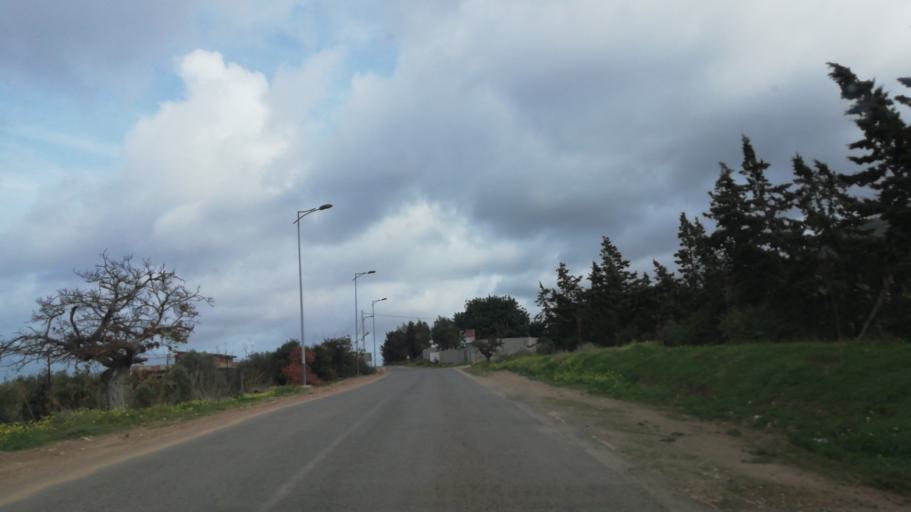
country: DZ
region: Oran
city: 'Ain el Turk
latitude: 35.6965
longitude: -0.8533
